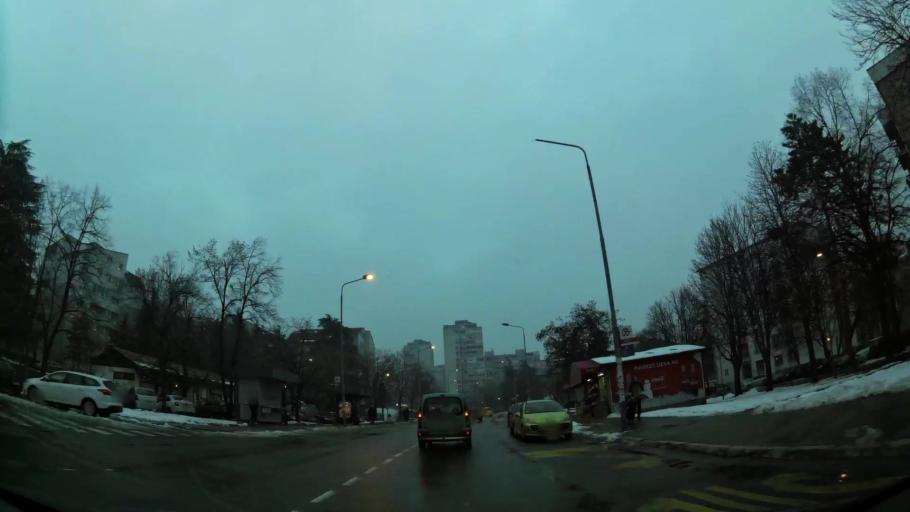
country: RS
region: Central Serbia
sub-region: Belgrade
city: Vozdovac
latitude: 44.7700
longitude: 20.4962
